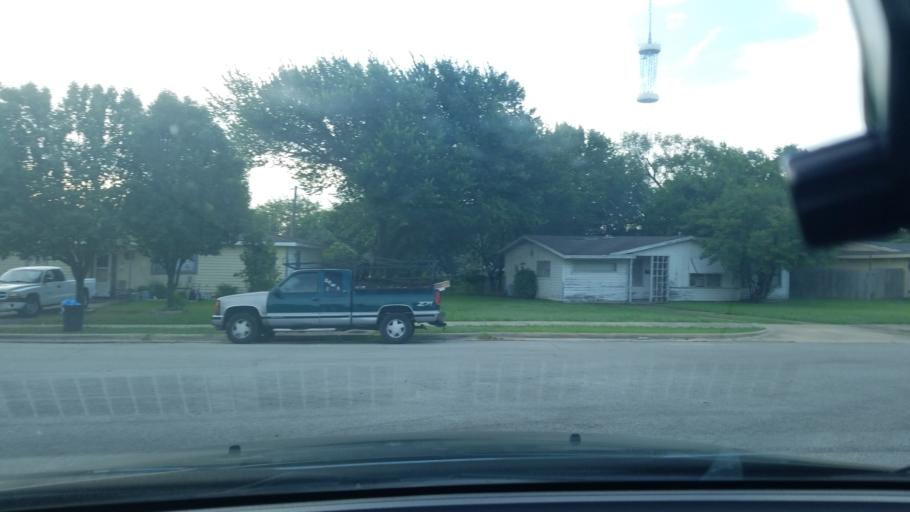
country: US
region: Texas
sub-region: Dallas County
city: Balch Springs
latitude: 32.7649
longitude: -96.6386
